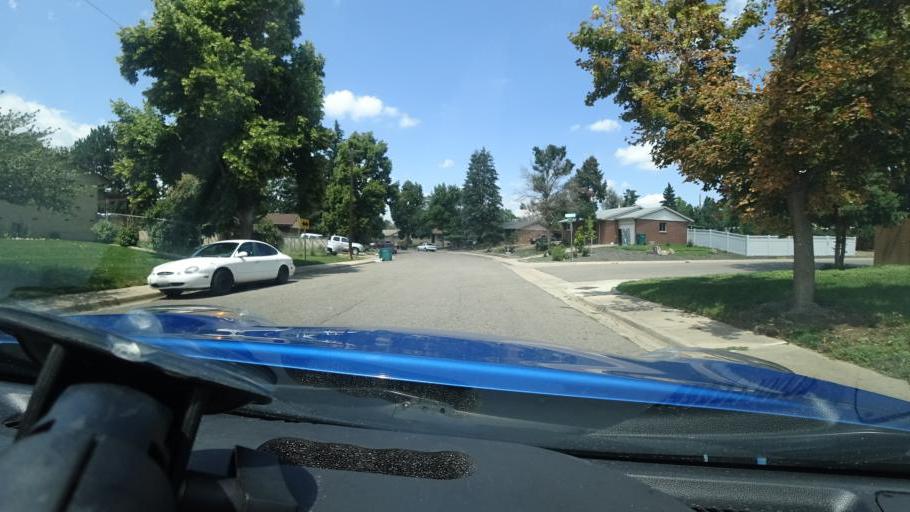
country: US
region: Colorado
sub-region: Adams County
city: Aurora
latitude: 39.7050
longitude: -104.8457
